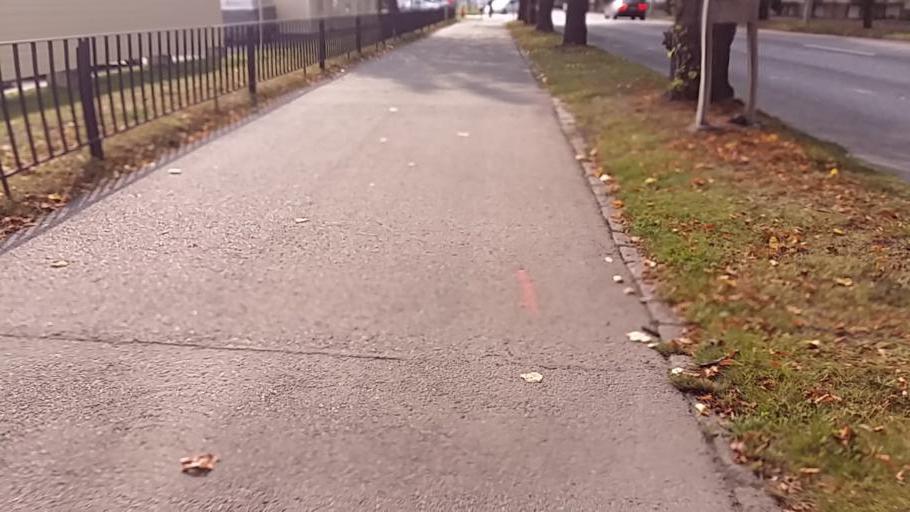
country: SE
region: Joenkoeping
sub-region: Jonkopings Kommun
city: Jonkoping
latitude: 57.7738
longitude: 14.1574
